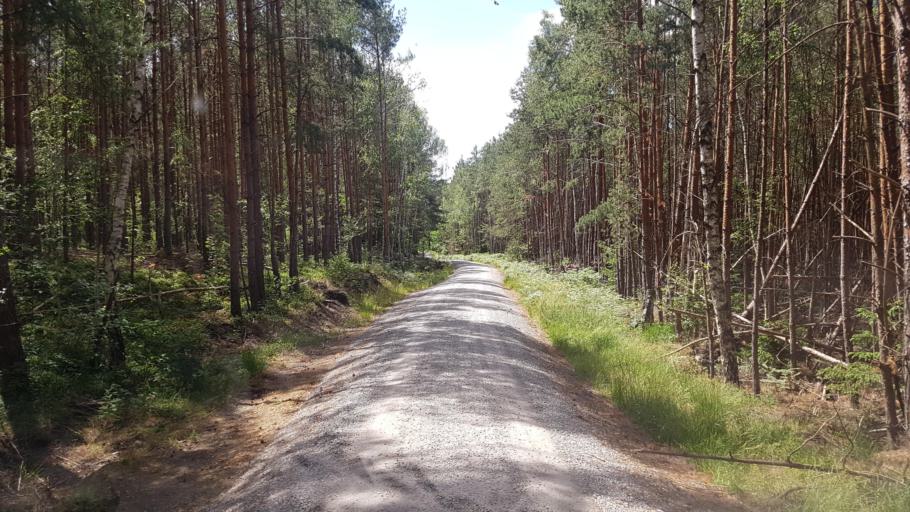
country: DE
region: Brandenburg
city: Plessa
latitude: 51.4944
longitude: 13.6083
